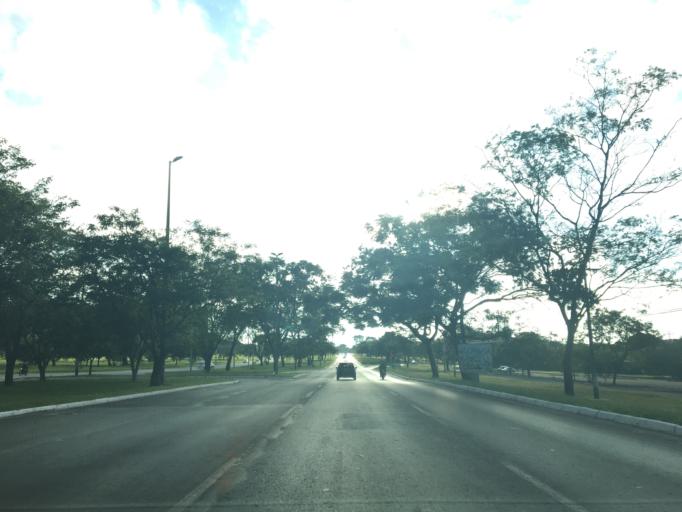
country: BR
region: Federal District
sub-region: Brasilia
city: Brasilia
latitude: -15.8157
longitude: -47.8722
